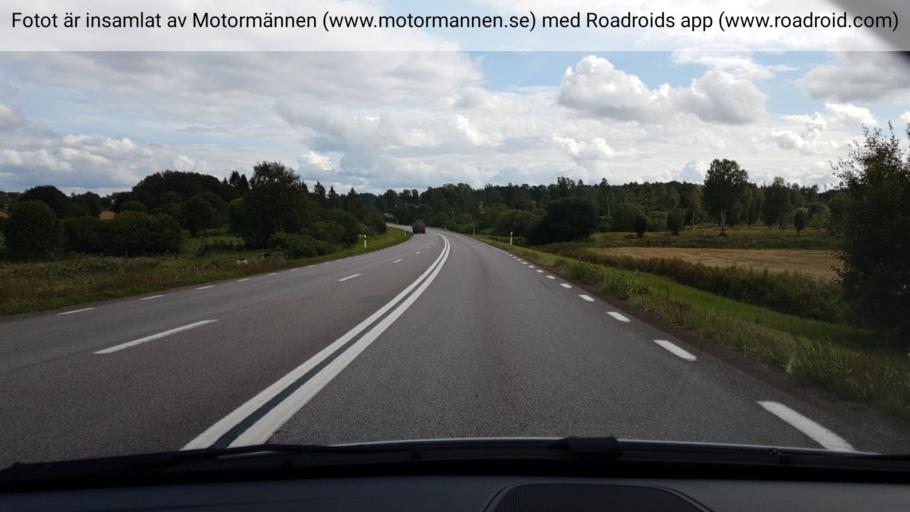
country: SE
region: Vaestra Goetaland
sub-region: Falkopings Kommun
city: Akarp
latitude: 58.1351
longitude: 13.6441
